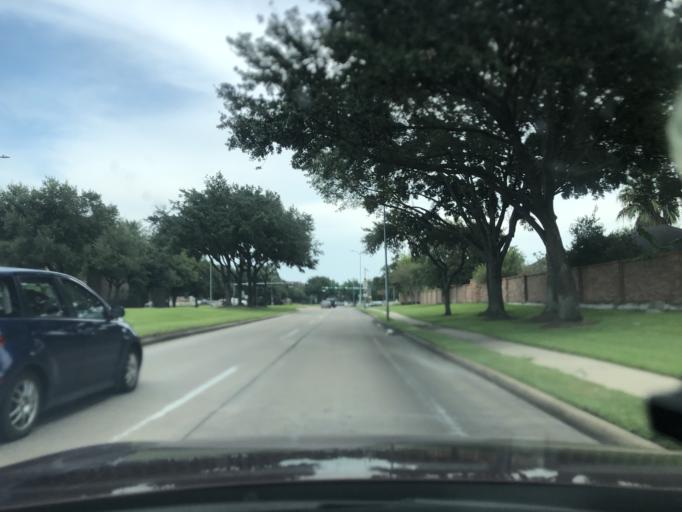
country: US
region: Texas
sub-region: Fort Bend County
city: Mission Bend
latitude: 29.7297
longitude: -95.6014
